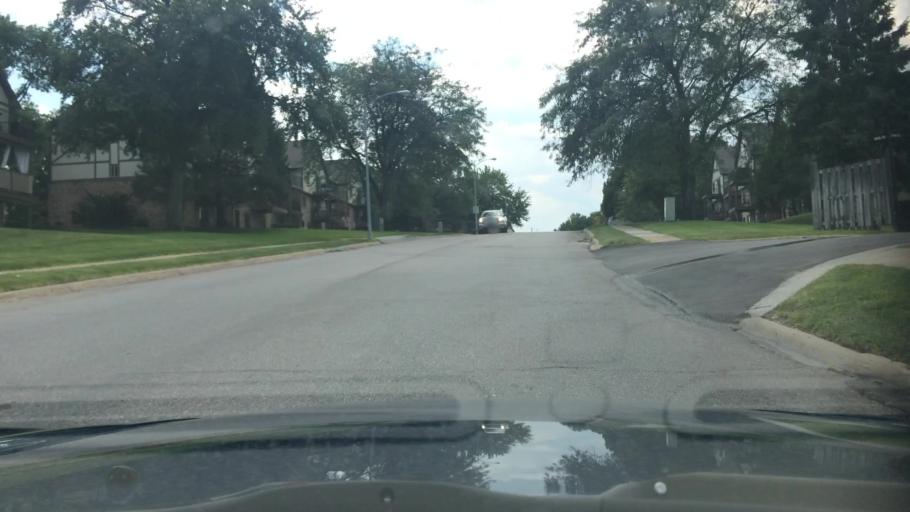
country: US
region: Nebraska
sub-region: Douglas County
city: Ralston
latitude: 41.2011
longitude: -96.0674
